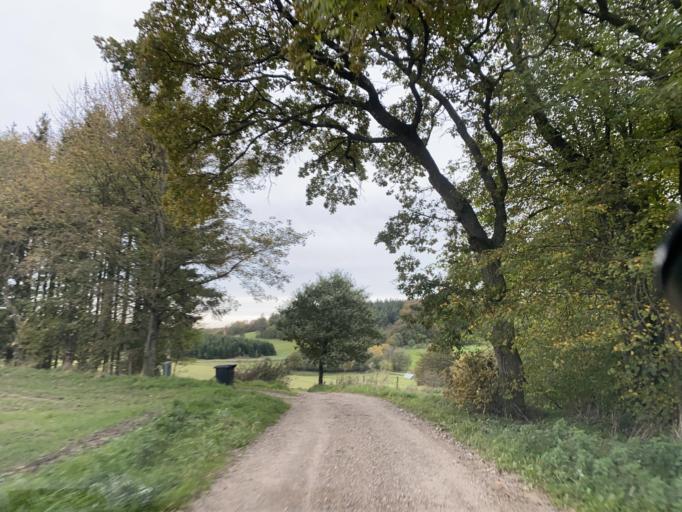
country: DK
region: Central Jutland
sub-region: Favrskov Kommune
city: Hammel
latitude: 56.1939
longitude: 9.7821
